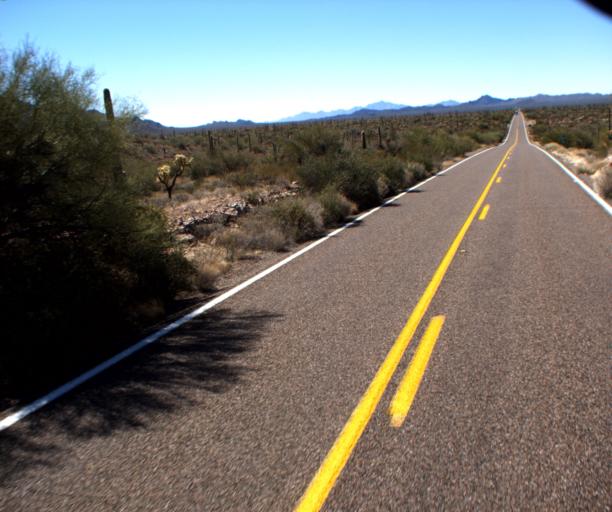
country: MX
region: Sonora
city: Sonoyta
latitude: 32.0835
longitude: -112.7780
